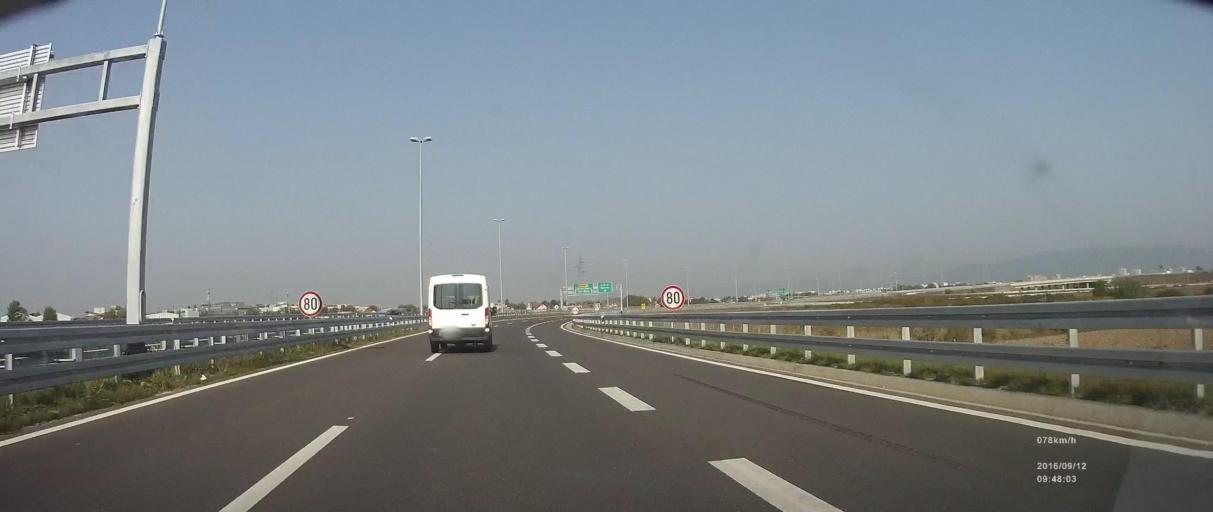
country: HR
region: Grad Zagreb
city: Odra
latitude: 45.7463
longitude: 16.0074
